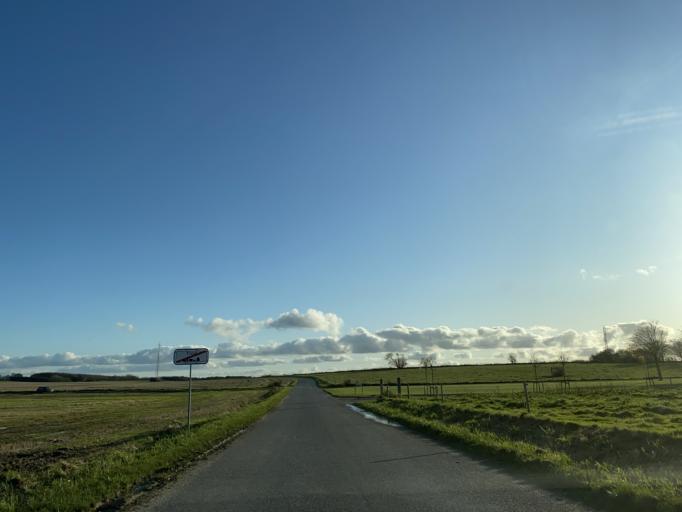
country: DK
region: Central Jutland
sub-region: Viborg Kommune
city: Bjerringbro
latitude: 56.3531
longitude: 9.7171
